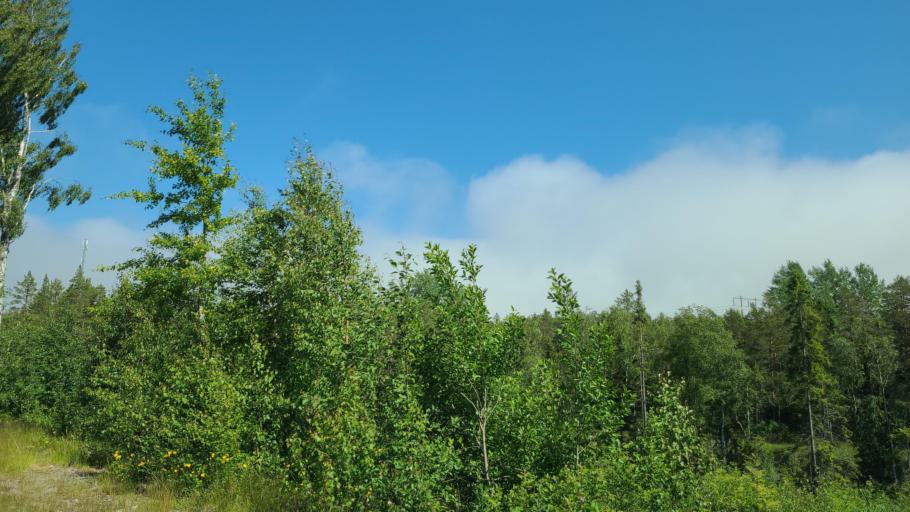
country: SE
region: Vaesternorrland
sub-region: OErnskoeldsviks Kommun
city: Husum
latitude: 63.4451
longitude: 19.2362
